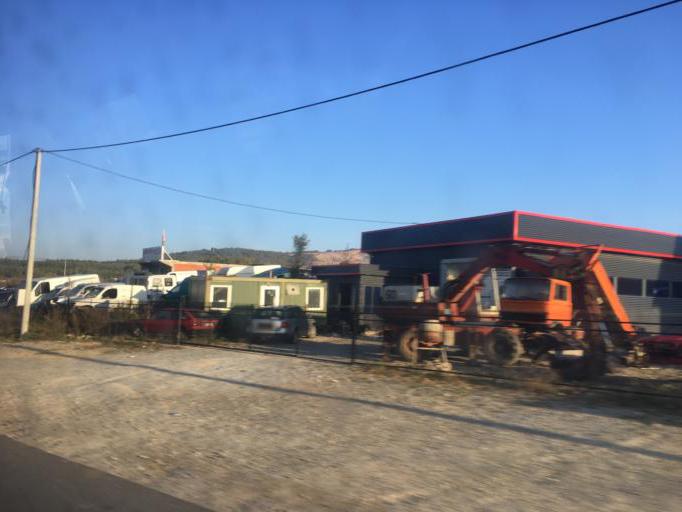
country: XK
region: Pristina
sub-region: Komuna e Drenasit
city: Glogovac
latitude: 42.6024
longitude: 20.9557
